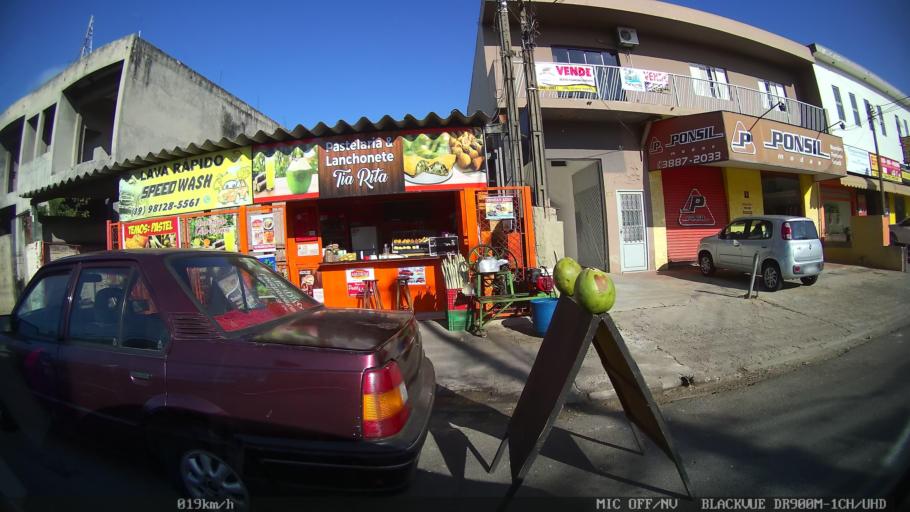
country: BR
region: Sao Paulo
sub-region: Hortolandia
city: Hortolandia
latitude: -22.8973
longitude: -47.1746
